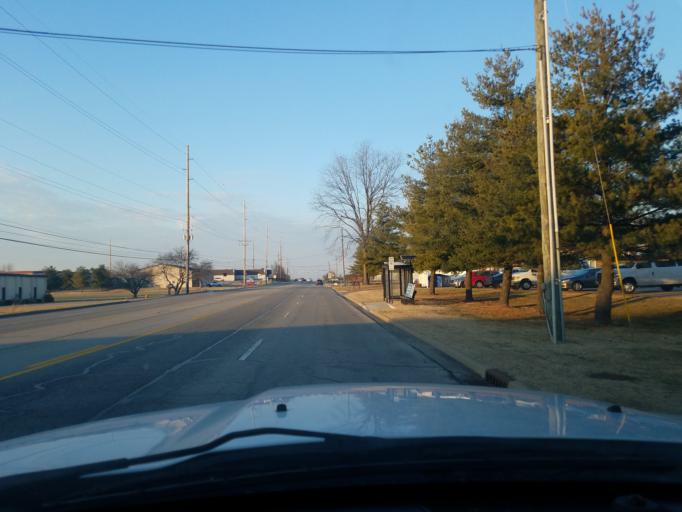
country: US
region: Indiana
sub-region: Vanderburgh County
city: Melody Hill
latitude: 37.9994
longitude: -87.4739
